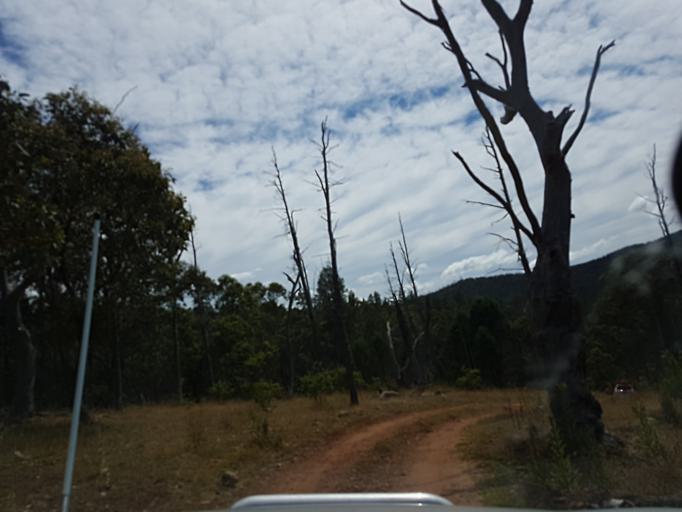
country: AU
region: New South Wales
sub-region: Snowy River
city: Jindabyne
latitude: -36.9402
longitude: 148.3964
